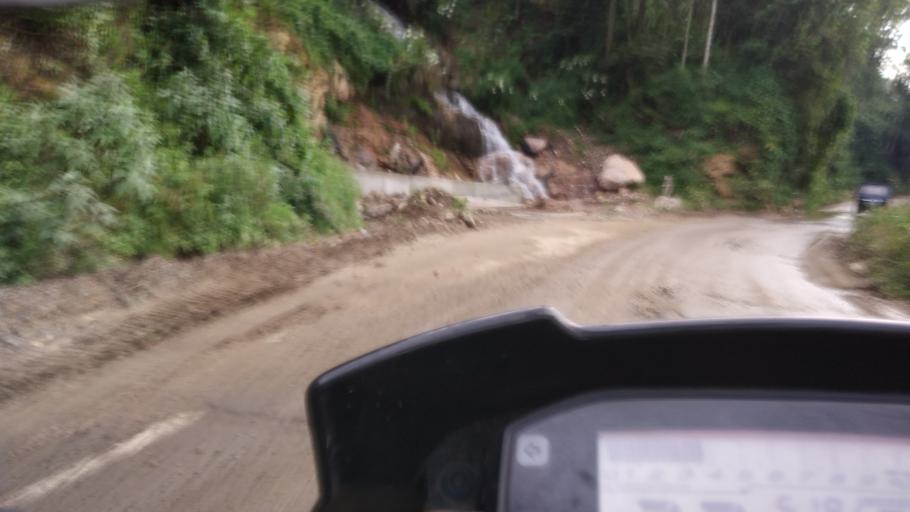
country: IN
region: Tamil Nadu
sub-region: Theni
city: Bodinayakkanur
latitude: 10.0213
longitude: 77.2483
